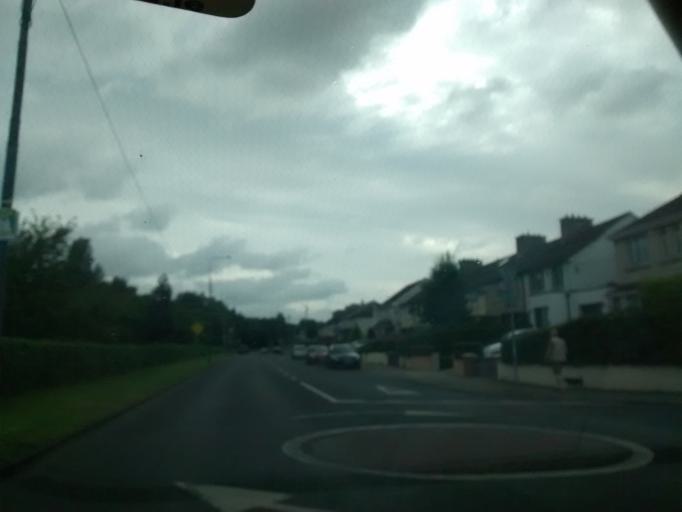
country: IE
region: Leinster
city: Dollymount
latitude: 53.3750
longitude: -6.1833
